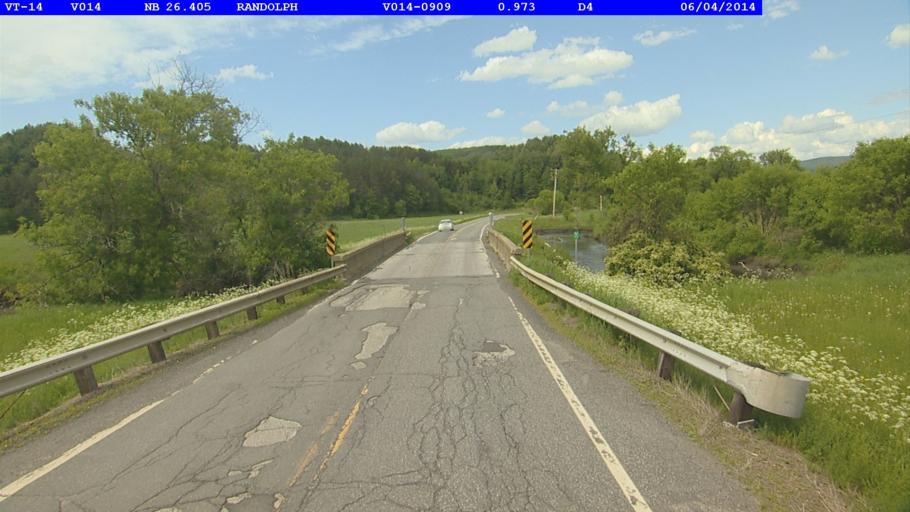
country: US
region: Vermont
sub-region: Orange County
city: Randolph
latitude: 43.8898
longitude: -72.5802
